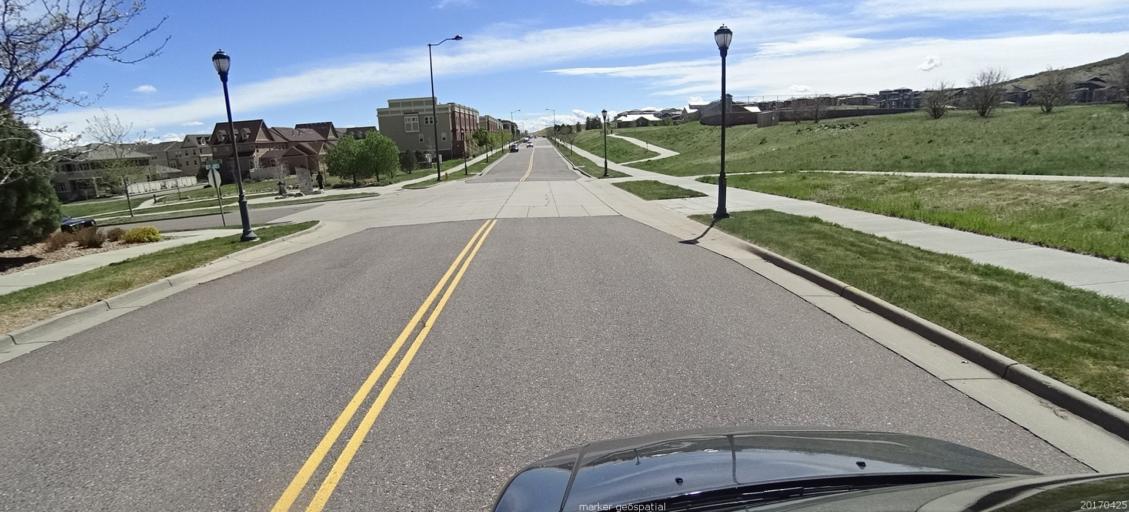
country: US
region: Colorado
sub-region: Douglas County
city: Carriage Club
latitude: 39.5285
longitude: -104.8820
